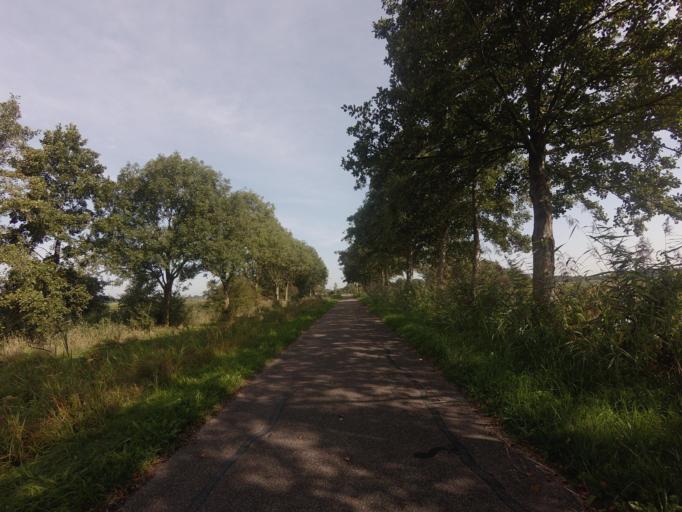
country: NL
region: Groningen
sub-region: Gemeente Leek
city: Leek
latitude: 53.1757
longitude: 6.4047
